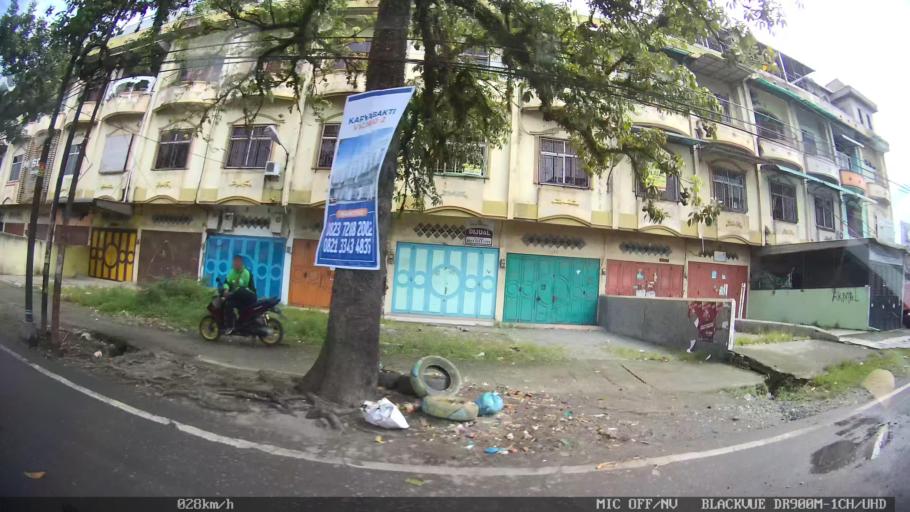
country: ID
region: North Sumatra
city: Medan
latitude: 3.6226
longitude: 98.7020
